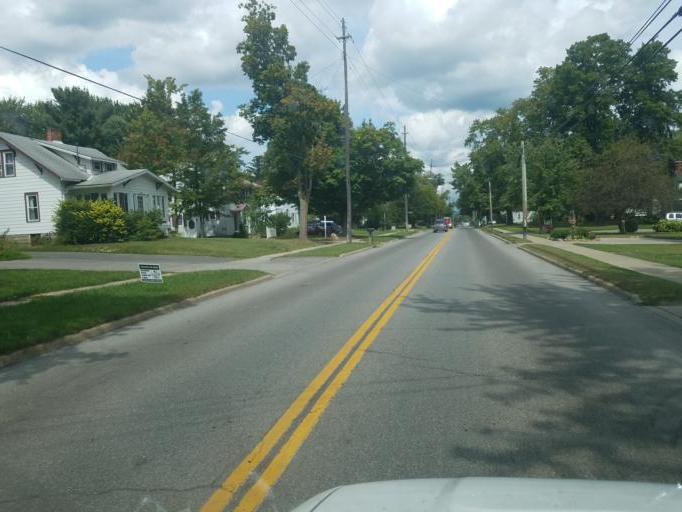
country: US
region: Ohio
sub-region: Geauga County
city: Middlefield
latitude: 41.4544
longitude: -81.0732
